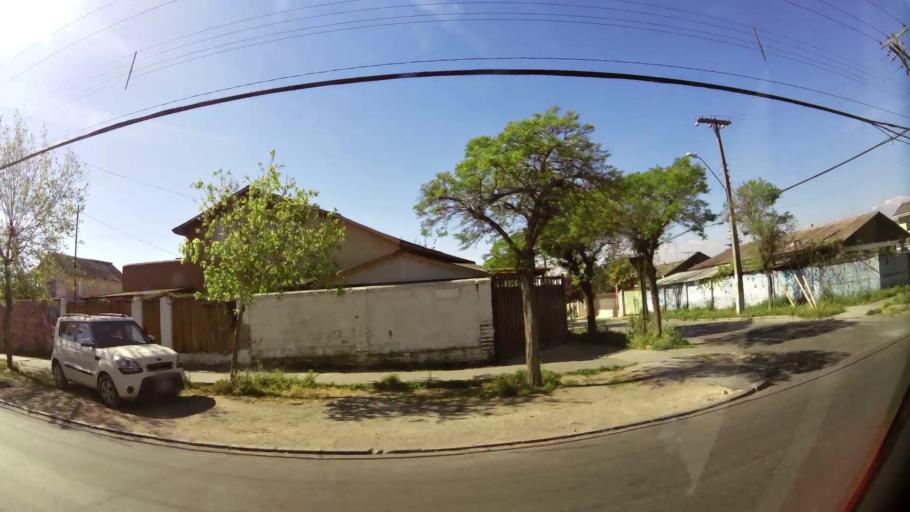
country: CL
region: Santiago Metropolitan
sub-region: Provincia de Santiago
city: Lo Prado
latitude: -33.4937
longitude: -70.7104
